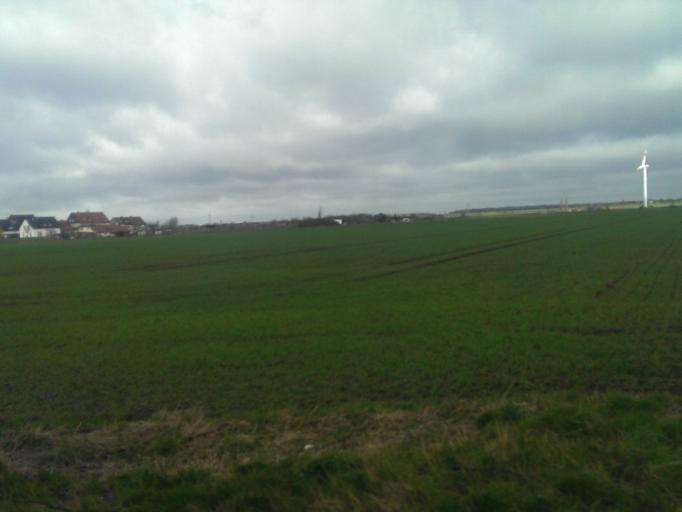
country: DE
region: Lower Saxony
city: Hildesheim
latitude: 52.1635
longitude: 10.0206
